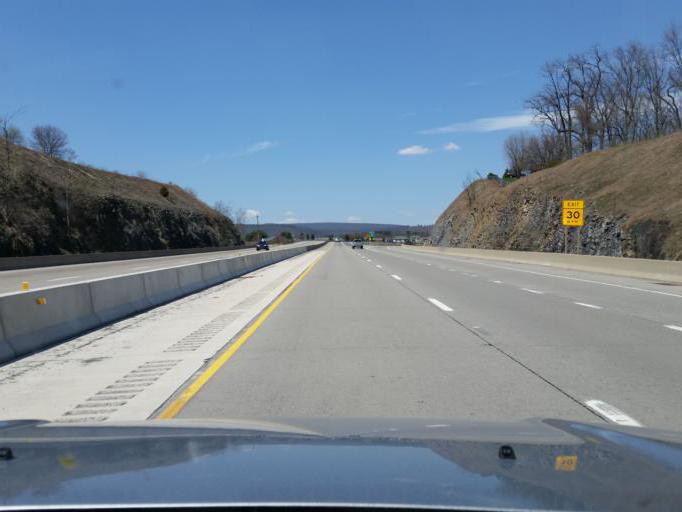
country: US
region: Pennsylvania
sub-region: Mifflin County
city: Church Hill
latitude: 40.6645
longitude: -77.6010
